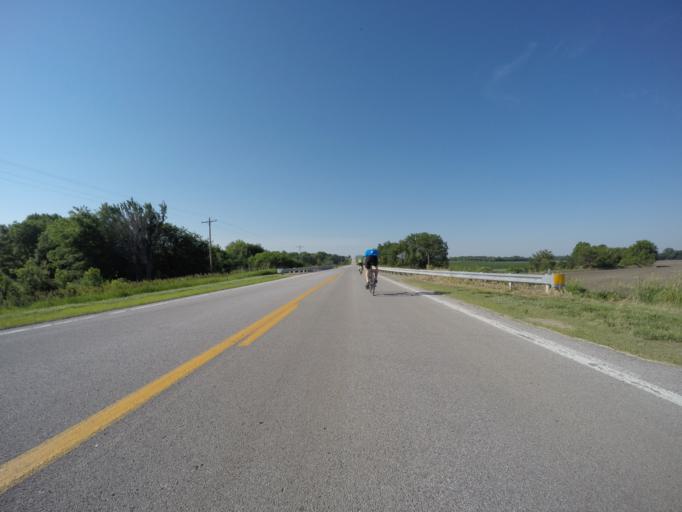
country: US
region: Nebraska
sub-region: Gage County
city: Wymore
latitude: 40.0809
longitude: -96.4827
